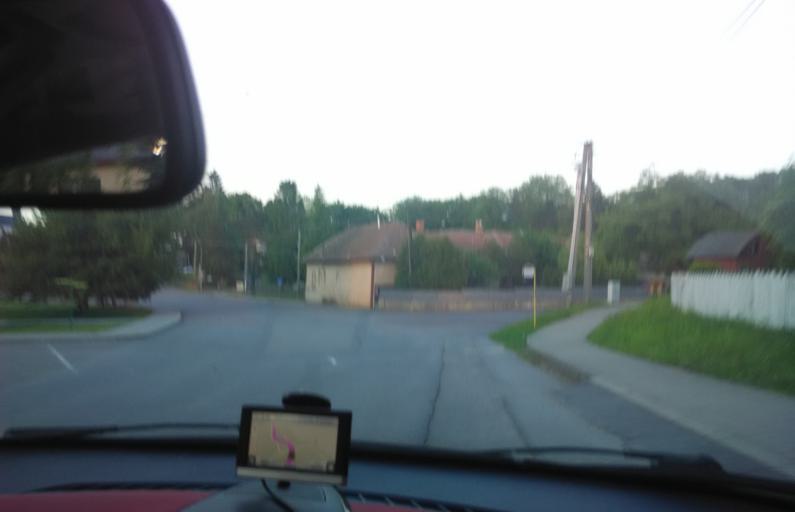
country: SK
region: Presovsky
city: Sabinov
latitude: 49.0801
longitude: 21.0815
